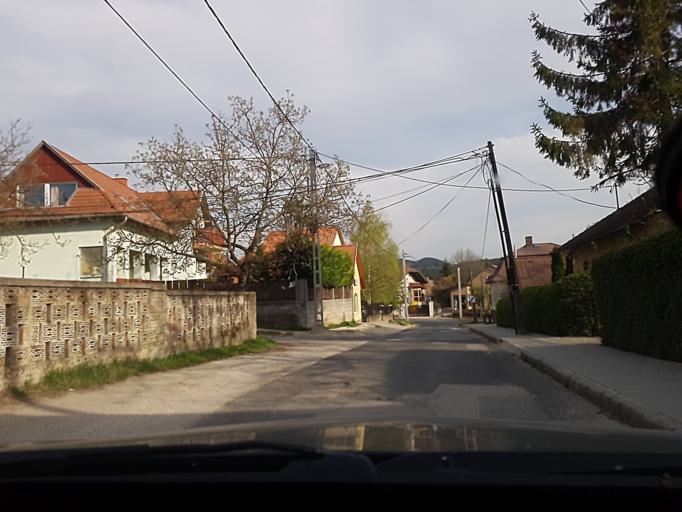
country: HU
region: Pest
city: Piliscsaba
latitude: 47.6347
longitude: 18.8262
